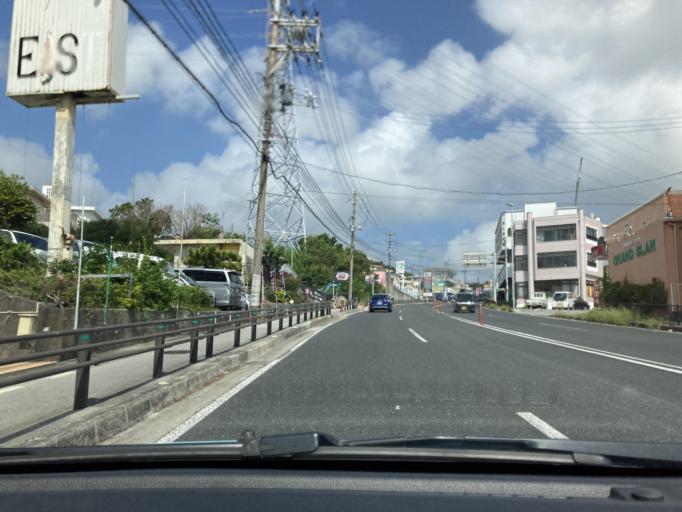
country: JP
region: Okinawa
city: Okinawa
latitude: 26.3277
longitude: 127.8224
